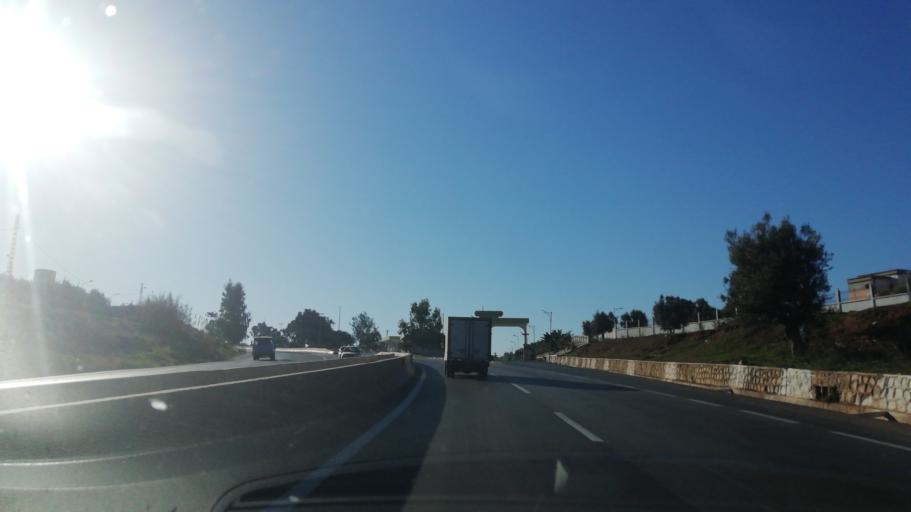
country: DZ
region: Tlemcen
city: Remchi
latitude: 35.0739
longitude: -1.4333
